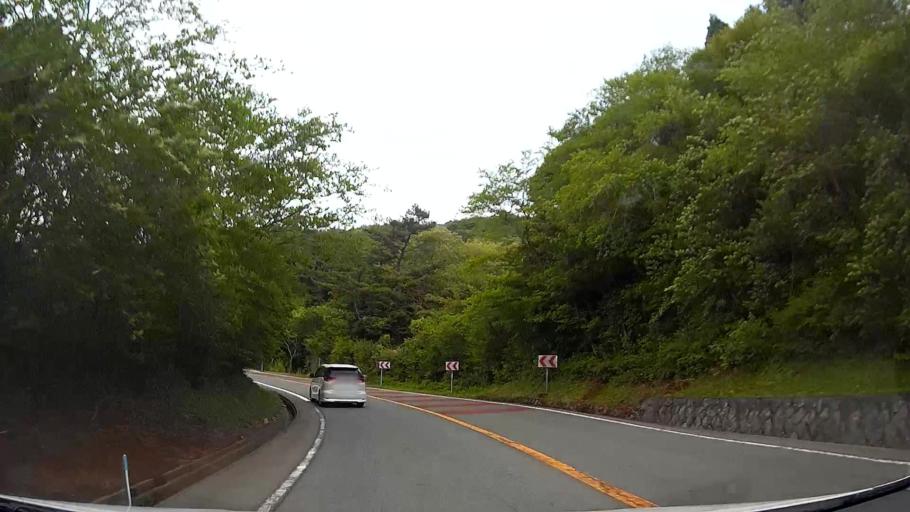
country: JP
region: Shizuoka
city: Atami
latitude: 35.0714
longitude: 139.0277
